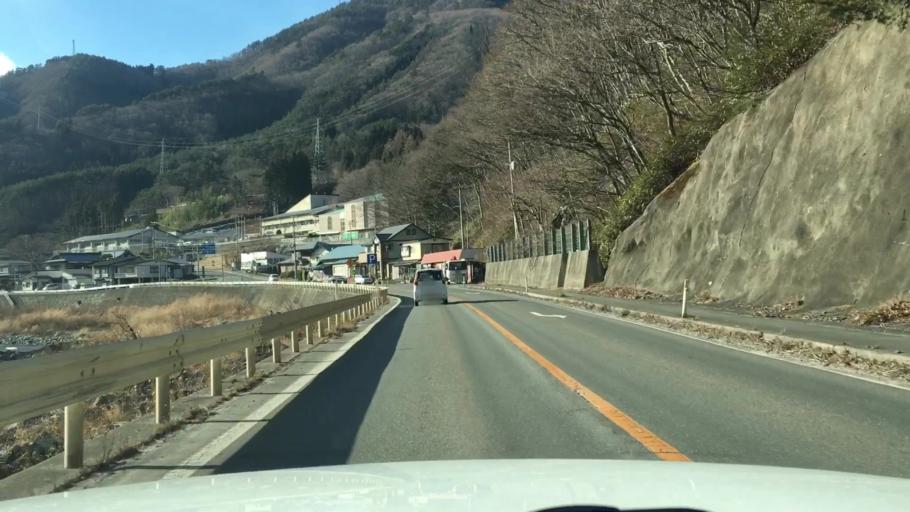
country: JP
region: Iwate
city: Miyako
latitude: 39.5998
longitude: 141.6833
